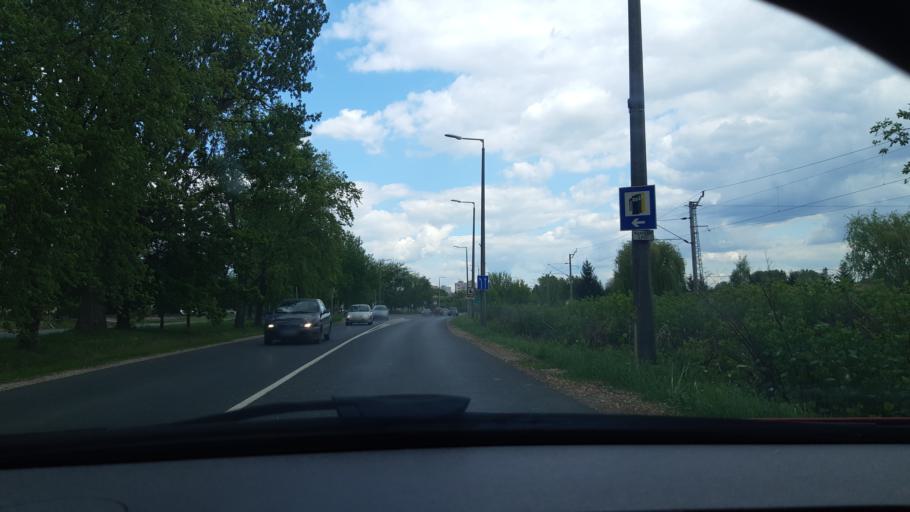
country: HU
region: Somogy
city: Kaposvar
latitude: 46.3661
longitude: 17.7626
